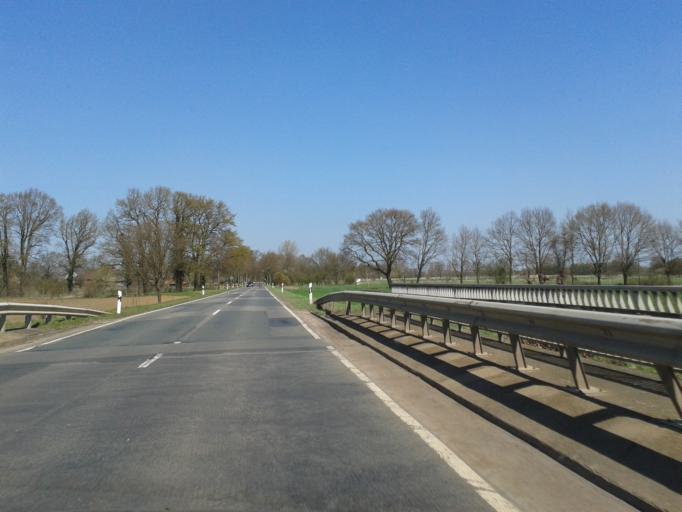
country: DE
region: Lower Saxony
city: Wustrow
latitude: 52.9314
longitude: 11.1150
